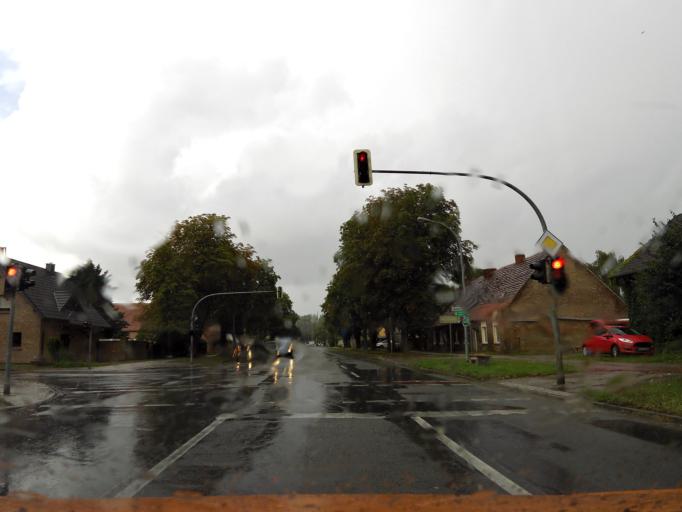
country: DE
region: Brandenburg
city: Wustermark
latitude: 52.4963
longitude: 12.9238
